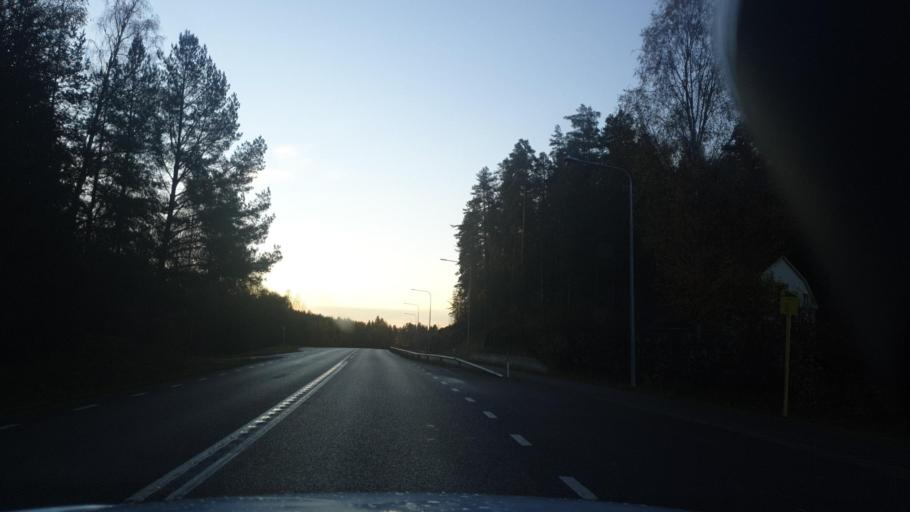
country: SE
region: Vaermland
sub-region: Arvika Kommun
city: Arvika
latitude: 59.6700
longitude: 12.5206
